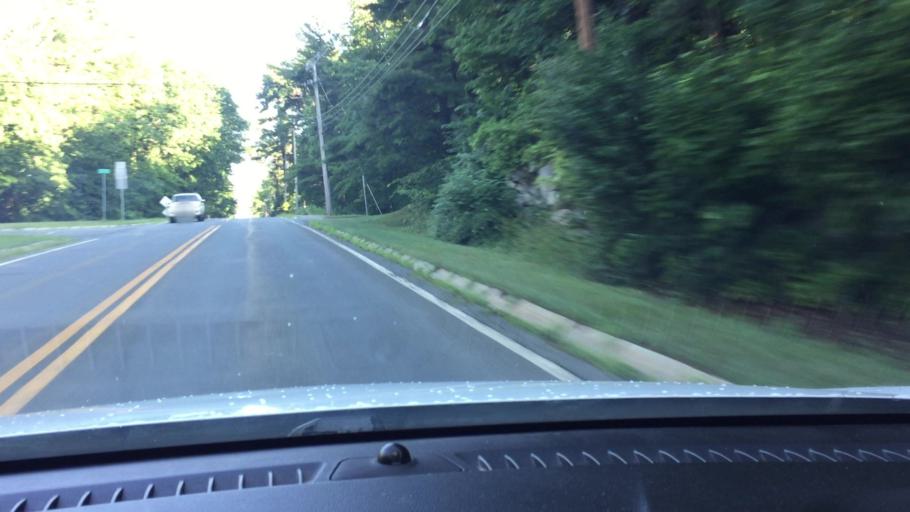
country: US
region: Massachusetts
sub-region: Berkshire County
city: Lenox
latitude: 42.3484
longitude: -73.2705
